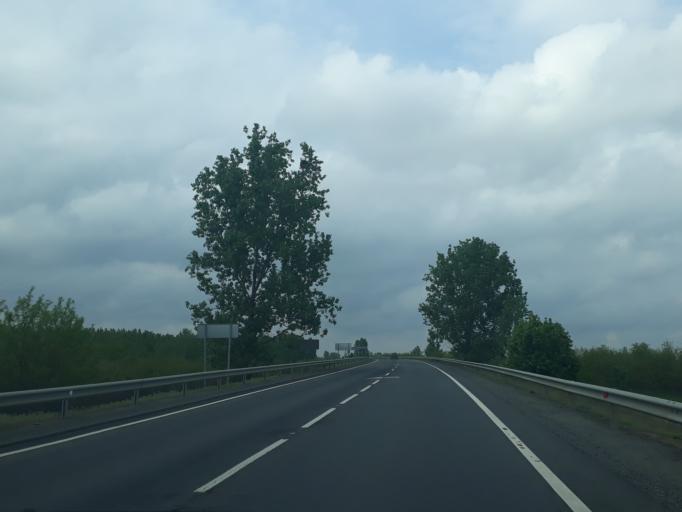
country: HU
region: Szabolcs-Szatmar-Bereg
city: Ajak
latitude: 48.1795
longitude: 22.0419
